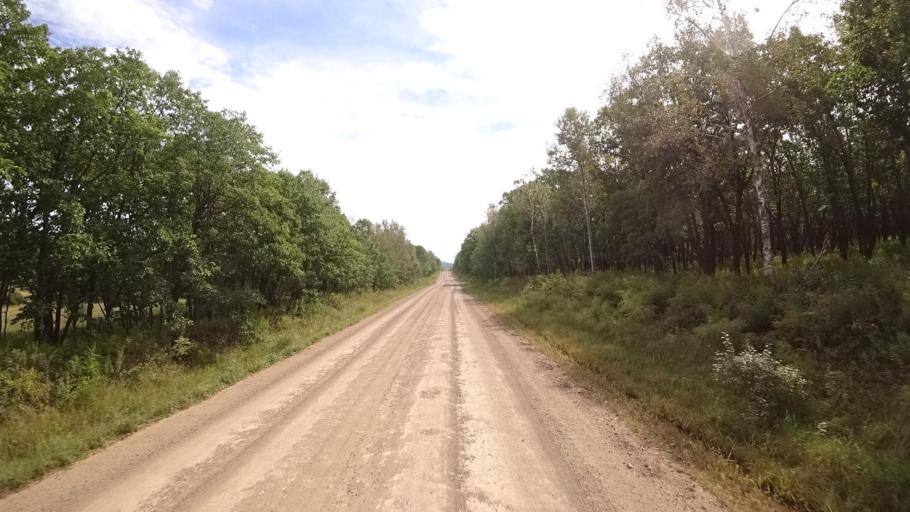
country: RU
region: Primorskiy
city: Yakovlevka
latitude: 44.6078
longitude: 133.6014
